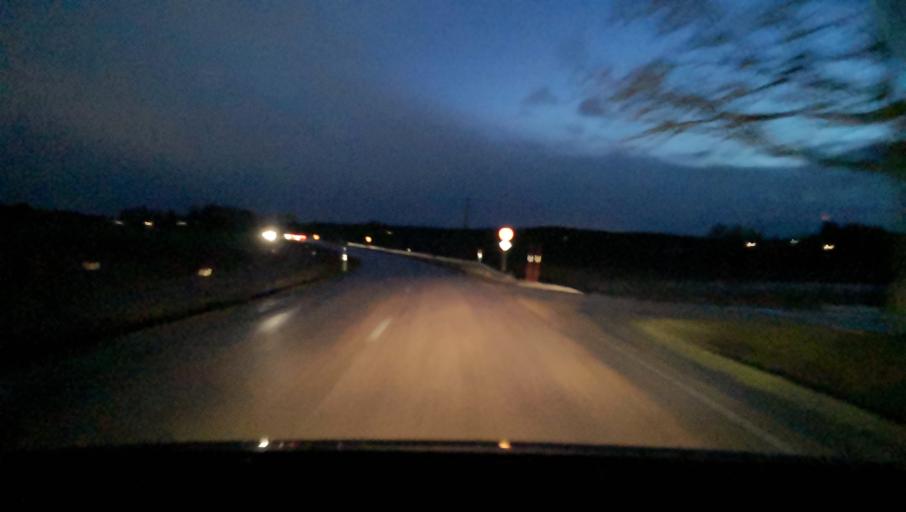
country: SE
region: Vaestmanland
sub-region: Vasteras
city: Skultuna
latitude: 59.6996
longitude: 16.4297
